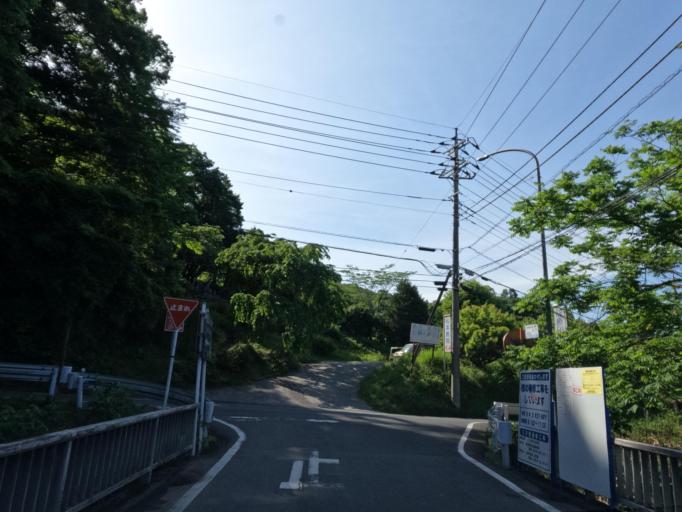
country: JP
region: Saitama
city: Chichibu
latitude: 36.0534
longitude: 139.1305
